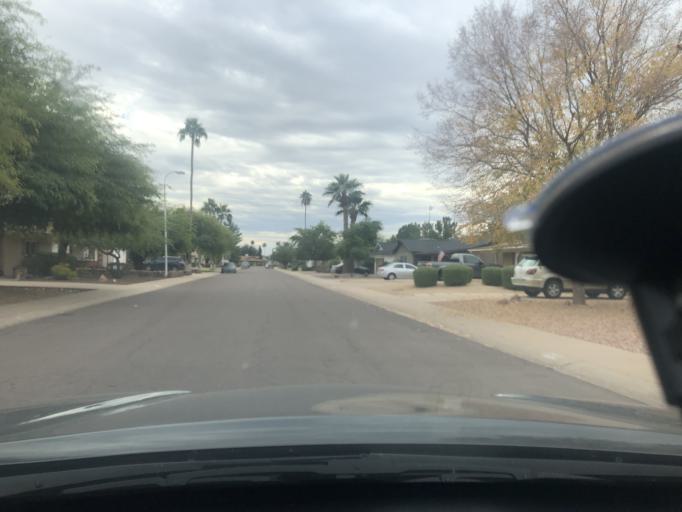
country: US
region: Arizona
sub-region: Maricopa County
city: Scottsdale
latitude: 33.4898
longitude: -111.8977
